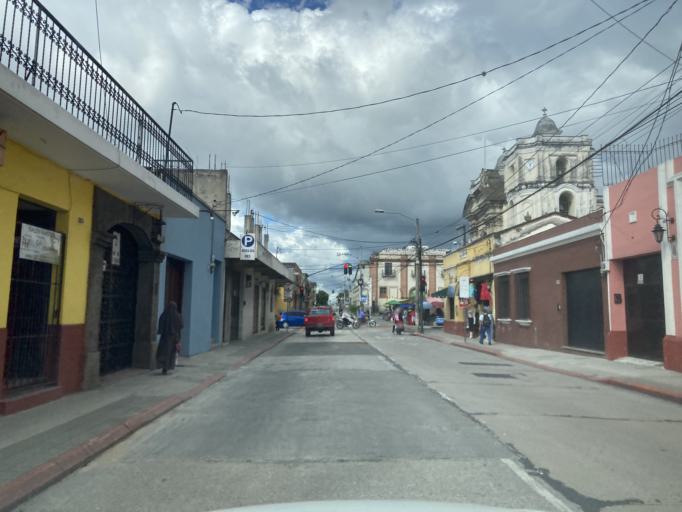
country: GT
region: Guatemala
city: Guatemala City
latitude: 14.6420
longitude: -90.5081
